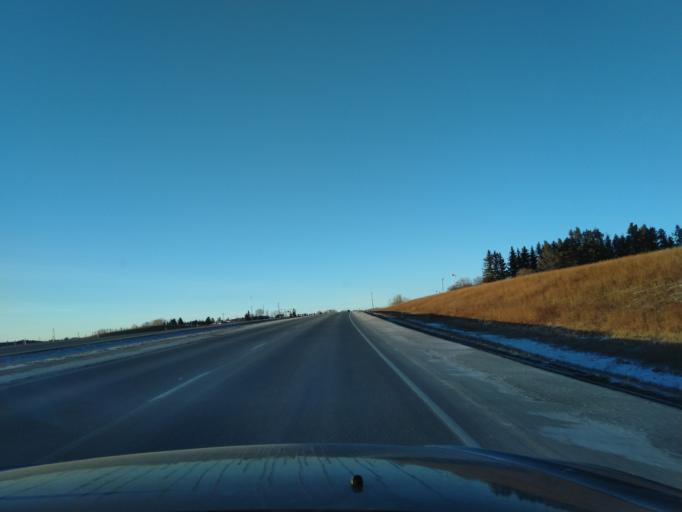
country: CA
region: Alberta
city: Cochrane
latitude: 51.1507
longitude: -114.2727
